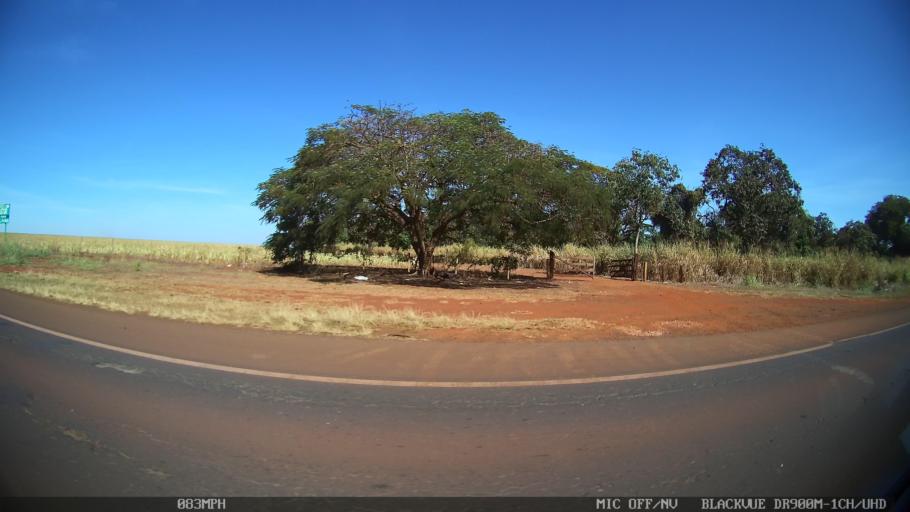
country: BR
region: Sao Paulo
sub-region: Guaira
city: Guaira
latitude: -20.4481
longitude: -48.1990
